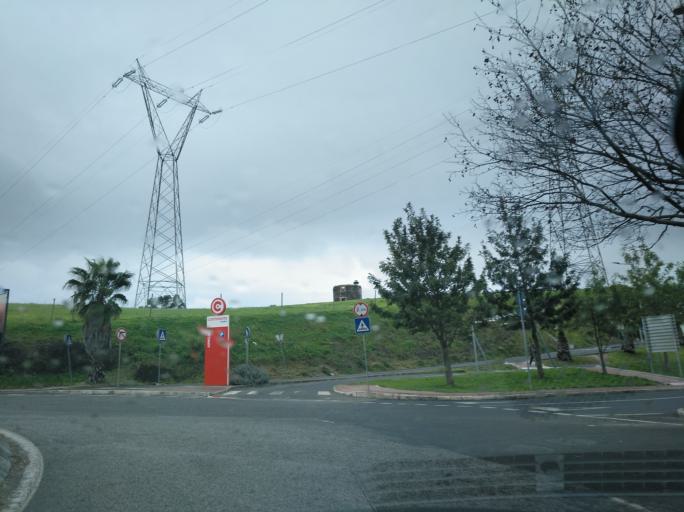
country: PT
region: Lisbon
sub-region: Odivelas
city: Odivelas
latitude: 38.7911
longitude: -9.1949
